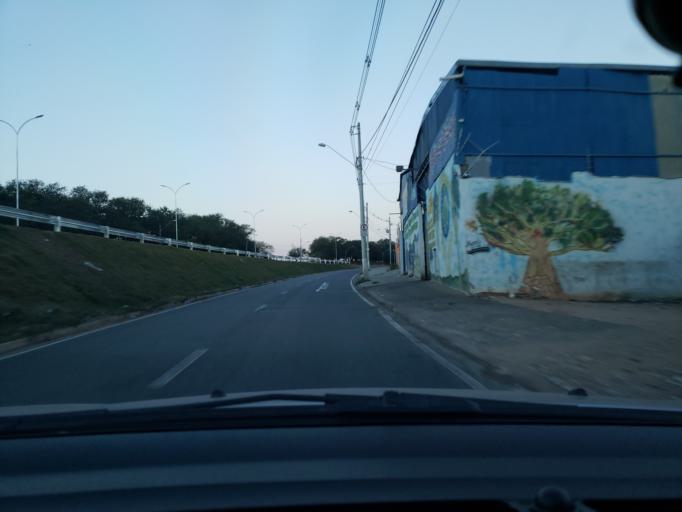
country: BR
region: Sao Paulo
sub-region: Campinas
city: Campinas
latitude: -22.9365
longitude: -47.1406
